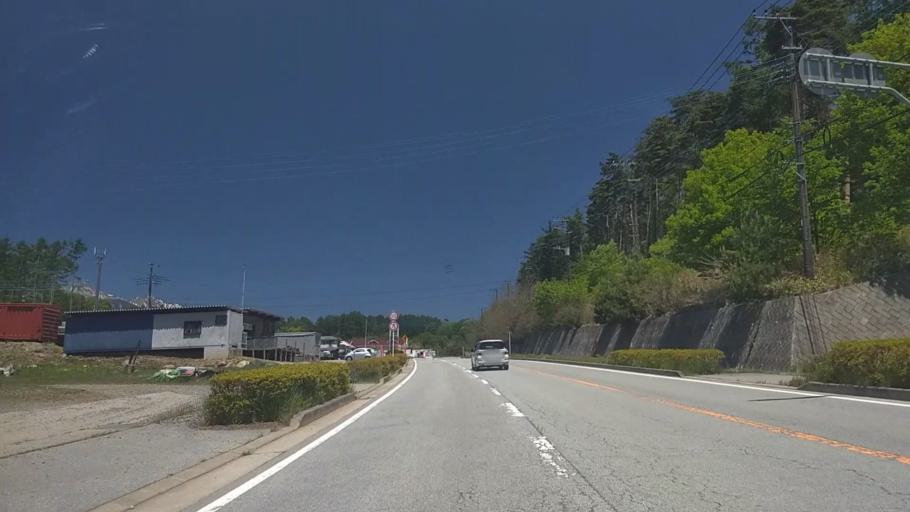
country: JP
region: Yamanashi
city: Nirasaki
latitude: 35.8868
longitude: 138.4395
